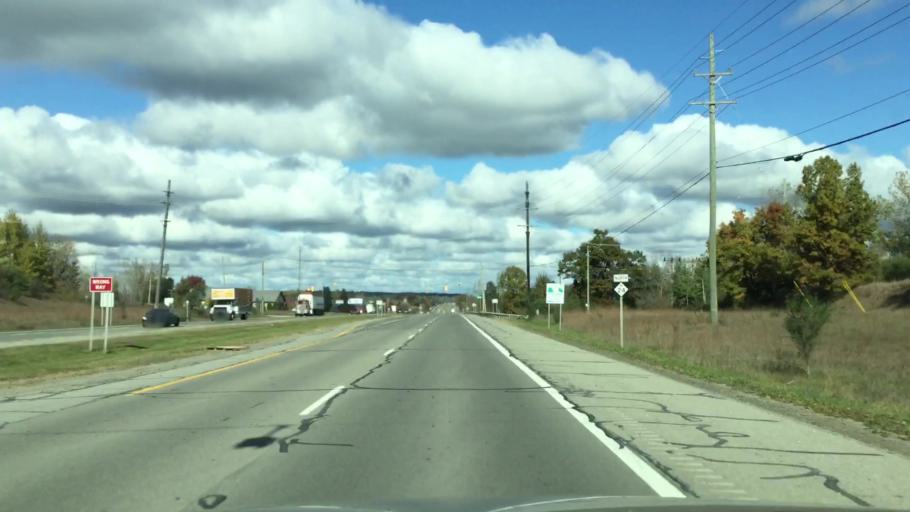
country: US
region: Michigan
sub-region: Oakland County
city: Oxford
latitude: 42.8478
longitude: -83.2791
